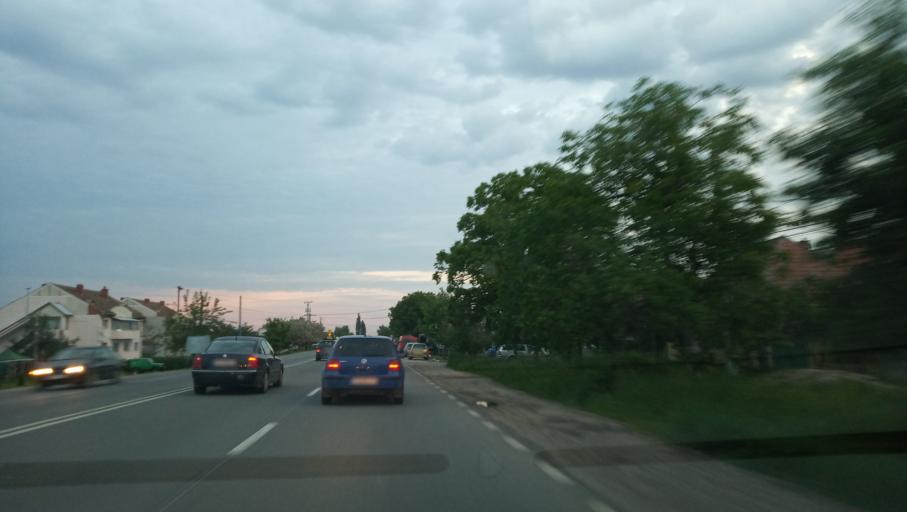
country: RO
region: Timis
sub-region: Comuna Sag
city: Sag
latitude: 45.6522
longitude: 21.1743
